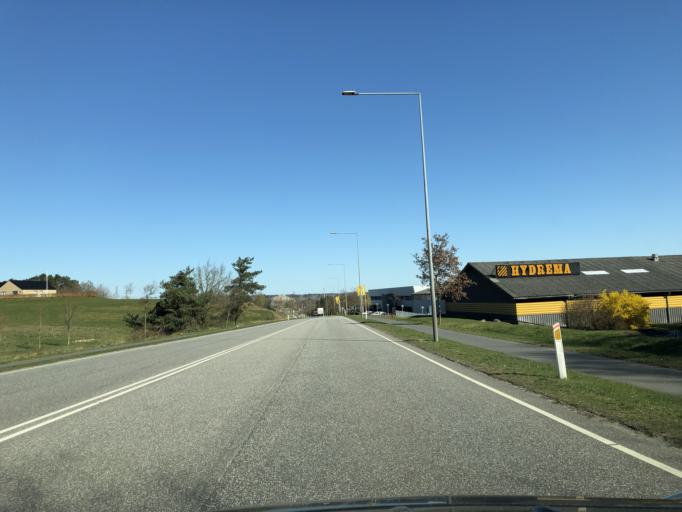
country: DK
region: North Denmark
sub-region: Rebild Kommune
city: Stovring
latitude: 56.8736
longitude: 9.8388
